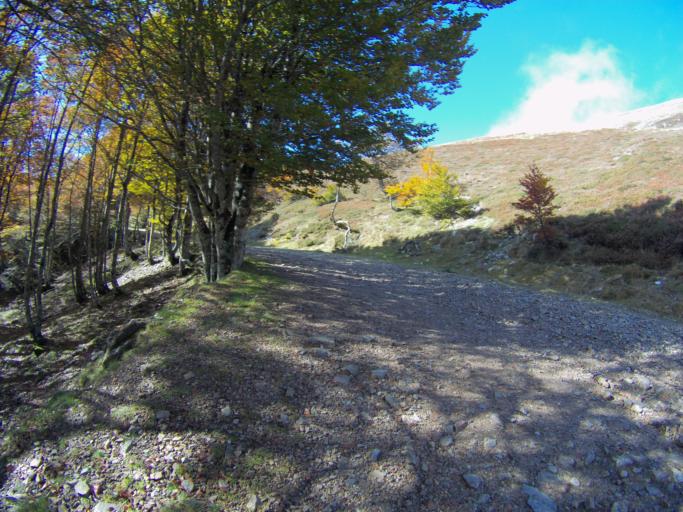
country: ES
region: Navarre
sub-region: Provincia de Navarra
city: Orbara
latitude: 43.0361
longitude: -1.2915
